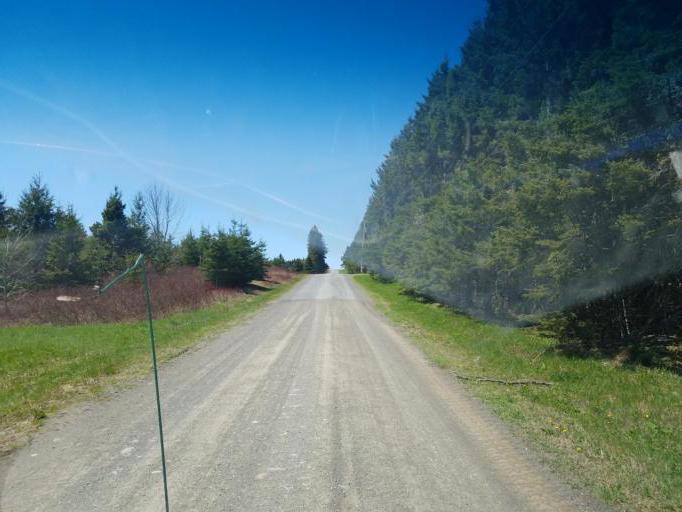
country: US
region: Maine
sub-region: Aroostook County
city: Caribou
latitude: 46.8675
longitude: -68.1883
